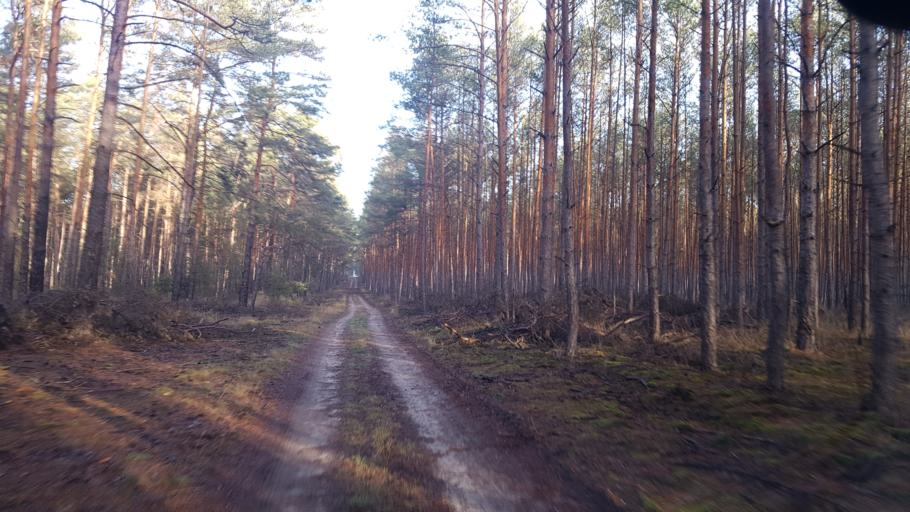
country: DE
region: Brandenburg
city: Schilda
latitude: 51.6301
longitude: 13.3945
